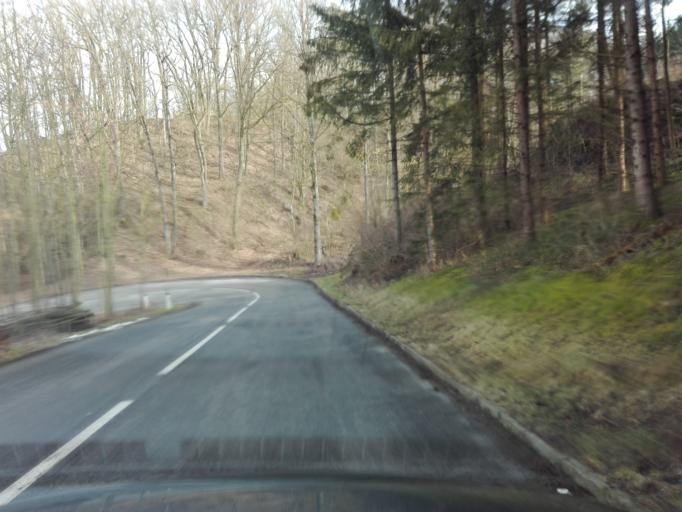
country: AT
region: Lower Austria
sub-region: Politischer Bezirk Amstetten
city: Ennsdorf
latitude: 48.2556
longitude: 14.4937
